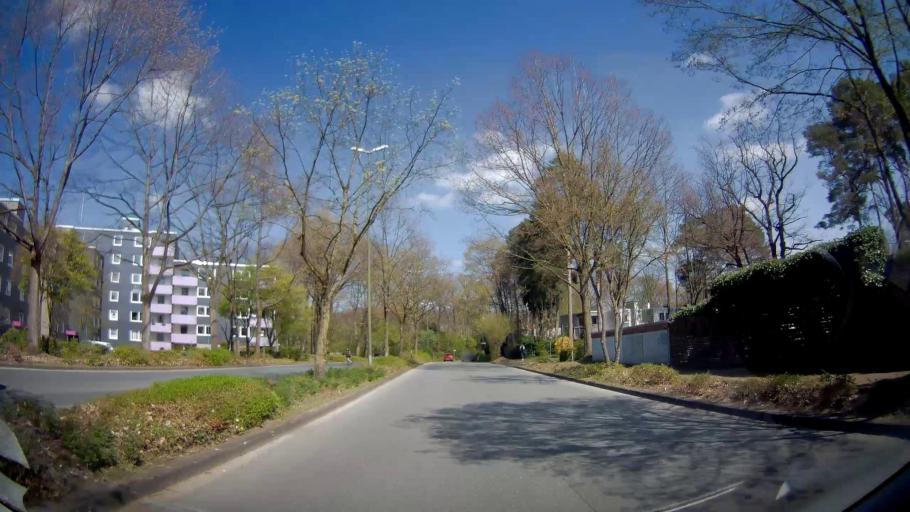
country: DE
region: North Rhine-Westphalia
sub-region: Regierungsbezirk Munster
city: Klein Reken
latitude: 51.7315
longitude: 7.0401
